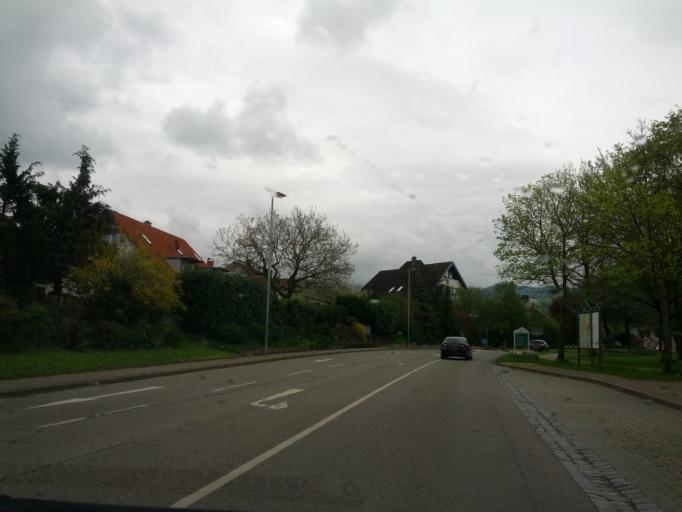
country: DE
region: Baden-Wuerttemberg
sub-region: Freiburg Region
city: Pfaffenweiler
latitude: 47.9187
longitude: 7.7461
